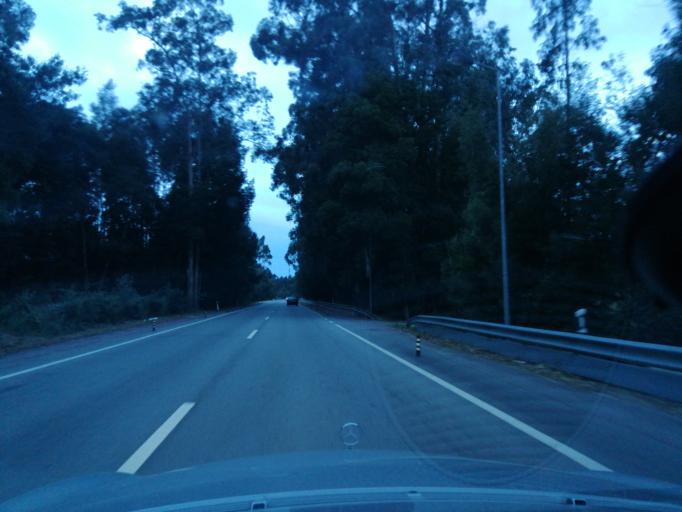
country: PT
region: Aveiro
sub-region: Estarreja
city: Estarreja
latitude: 40.7597
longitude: -8.6073
